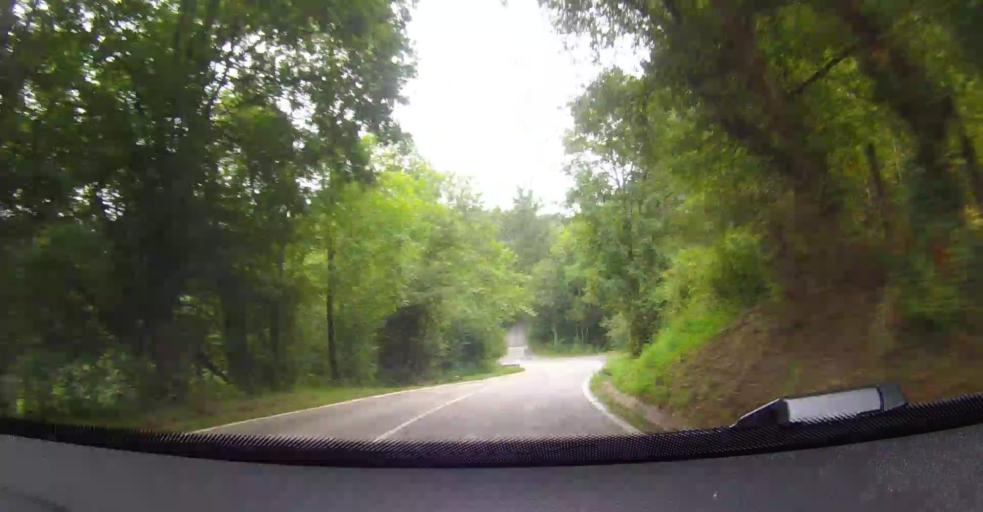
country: ES
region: Basque Country
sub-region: Bizkaia
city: Balmaseda
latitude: 43.2442
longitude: -3.2781
